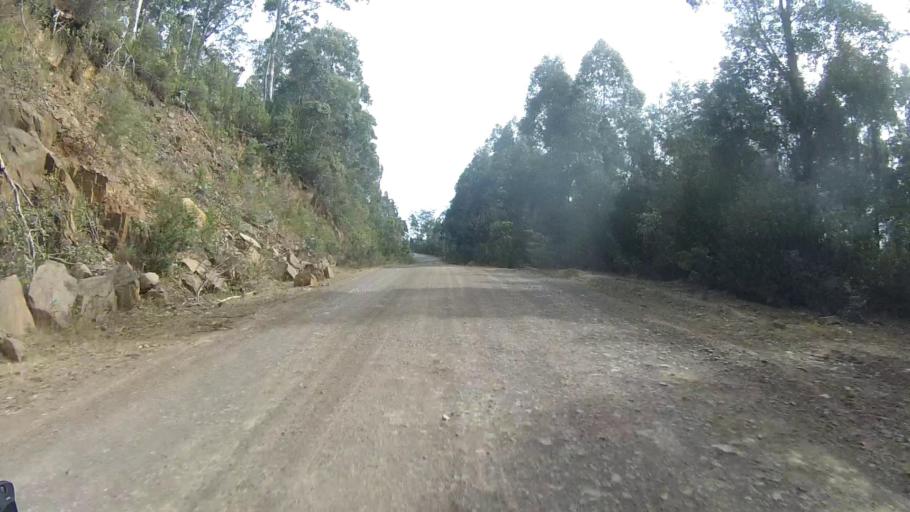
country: AU
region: Tasmania
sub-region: Sorell
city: Sorell
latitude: -42.7637
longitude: 147.8298
